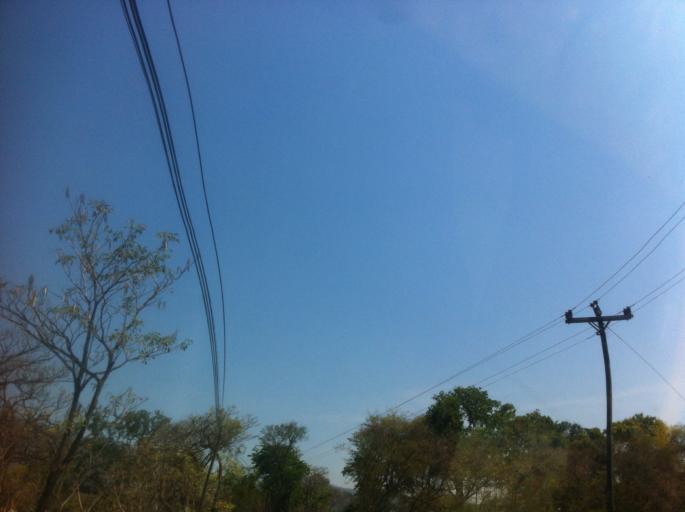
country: CR
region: Guanacaste
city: Hojancha
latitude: 10.0859
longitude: -85.4640
